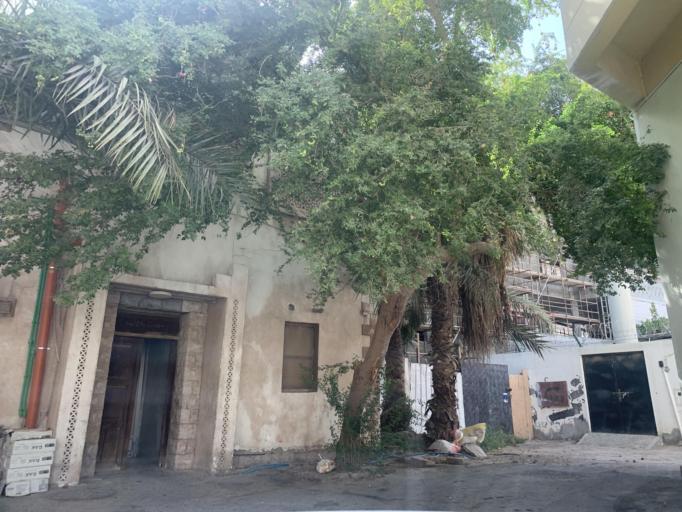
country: BH
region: Manama
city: Jidd Hafs
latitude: 26.2086
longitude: 50.5563
